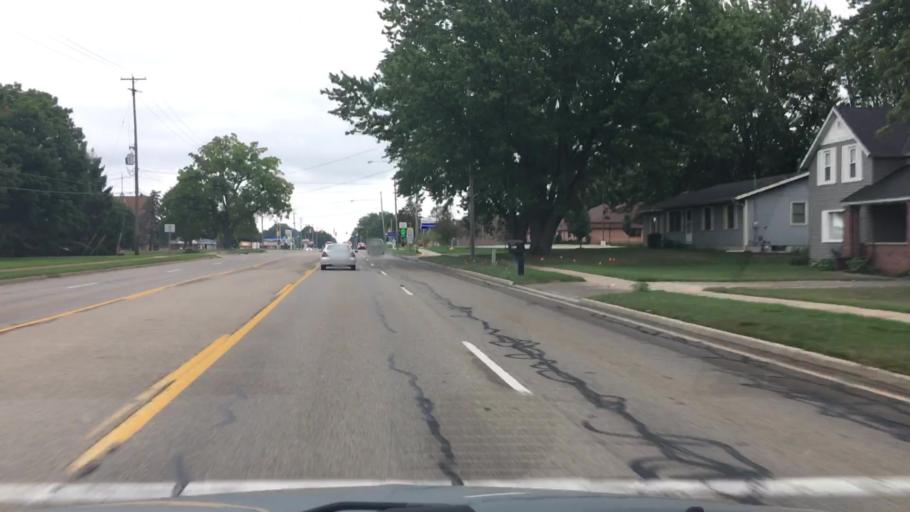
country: US
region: Michigan
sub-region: Ottawa County
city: Jenison
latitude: 42.9071
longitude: -85.8352
